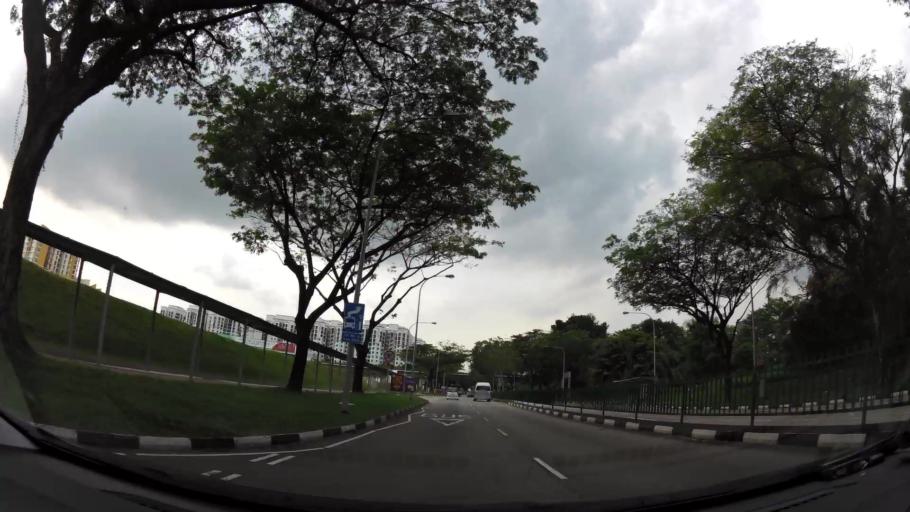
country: MY
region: Johor
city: Kampung Pasir Gudang Baru
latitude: 1.4479
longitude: 103.8223
